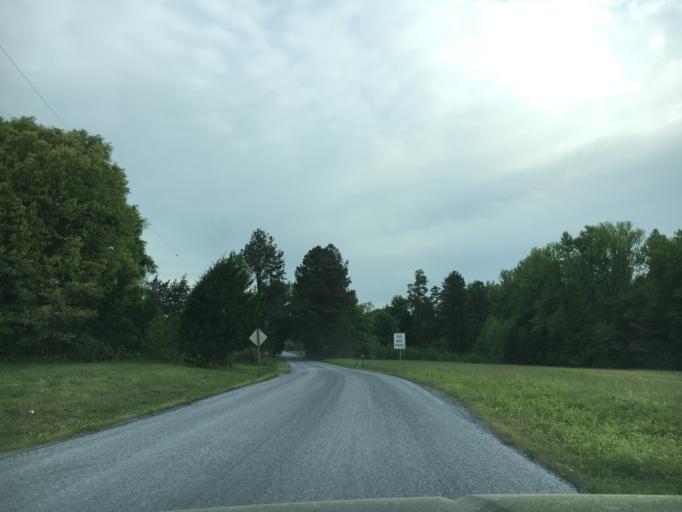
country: US
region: Virginia
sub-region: Campbell County
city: Brookneal
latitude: 36.9243
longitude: -78.9496
